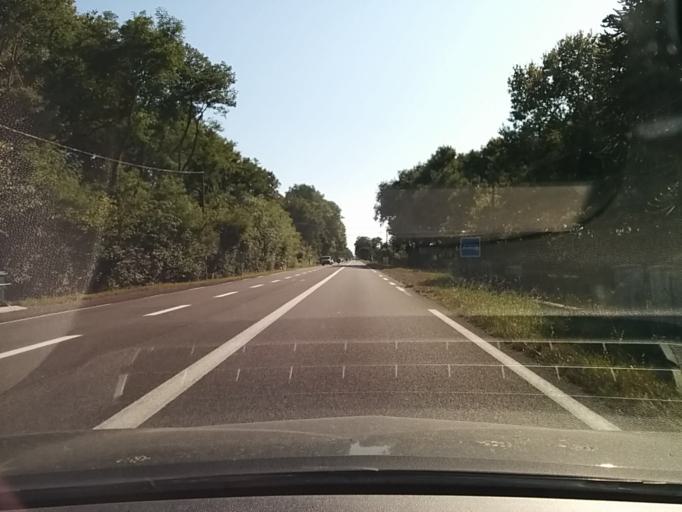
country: FR
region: Aquitaine
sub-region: Departement des Landes
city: Benesse-Maremne
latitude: 43.6418
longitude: -1.3427
